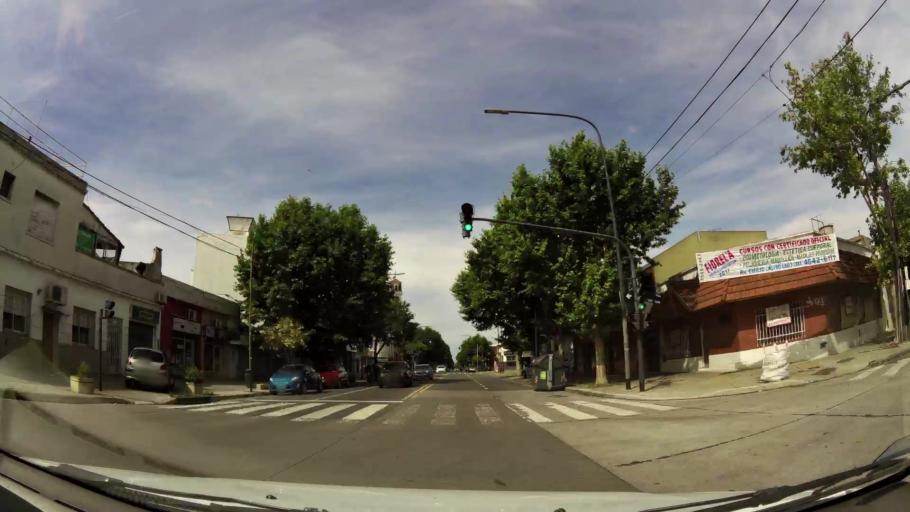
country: AR
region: Buenos Aires F.D.
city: Villa Lugano
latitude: -34.6510
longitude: -58.5135
